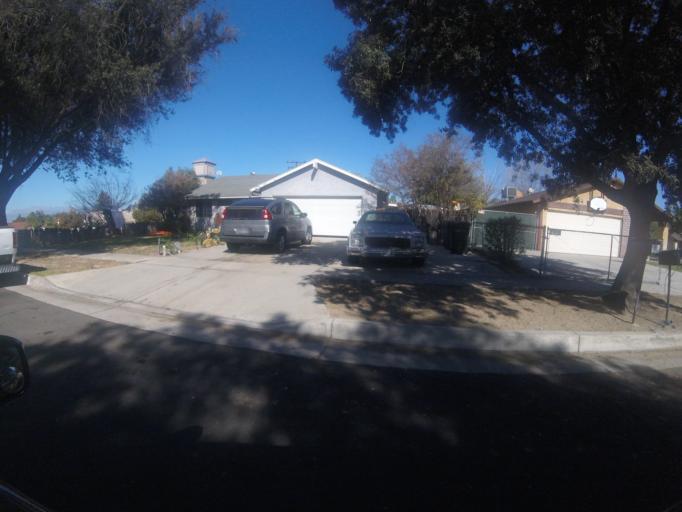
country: US
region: California
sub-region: San Bernardino County
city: Redlands
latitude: 34.0751
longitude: -117.1810
